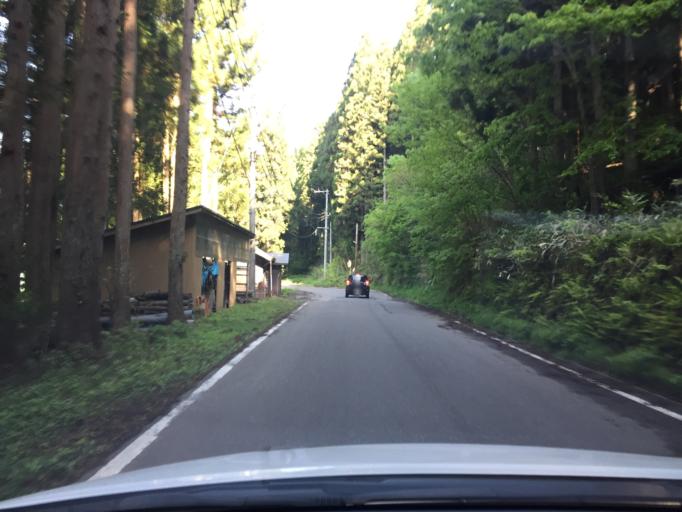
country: JP
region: Fukushima
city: Kitakata
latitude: 37.6672
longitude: 139.6109
